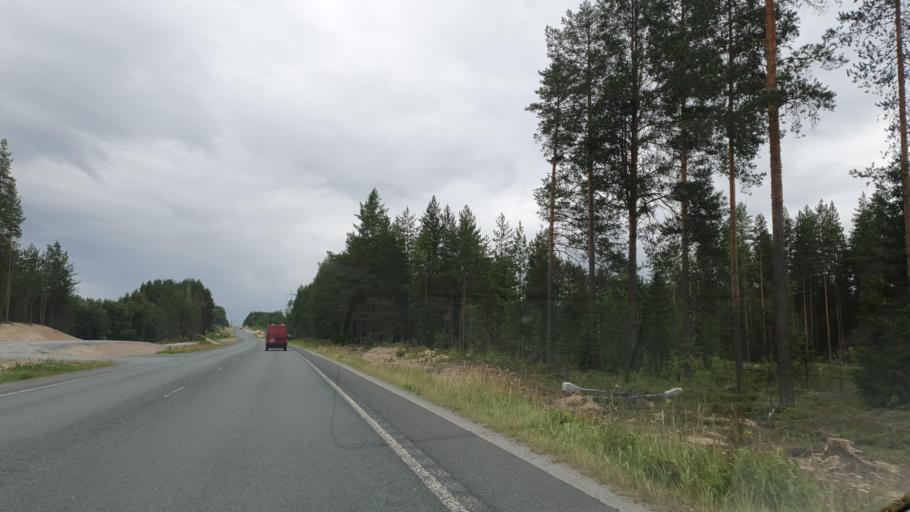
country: FI
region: Northern Savo
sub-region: Ylae-Savo
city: Lapinlahti
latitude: 63.2775
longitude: 27.4578
